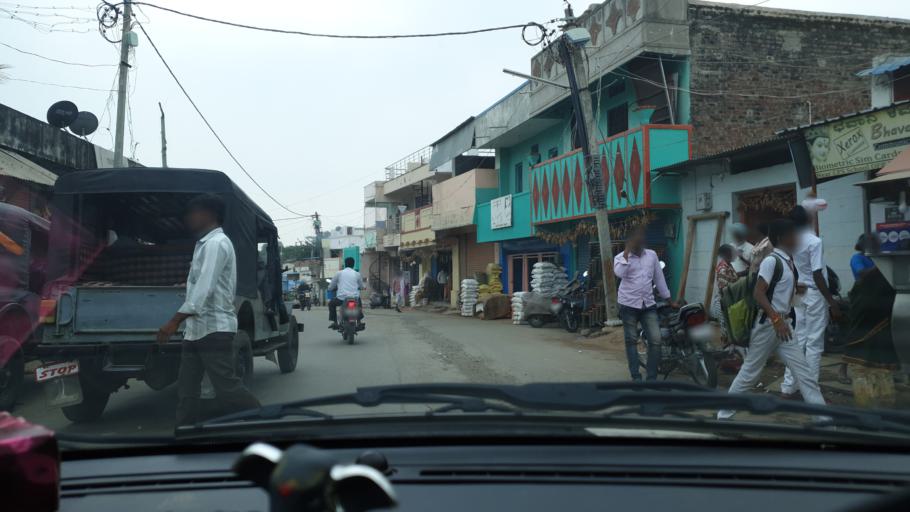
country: IN
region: Karnataka
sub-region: Yadgir
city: Gurmatkal
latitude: 16.8657
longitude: 77.3930
